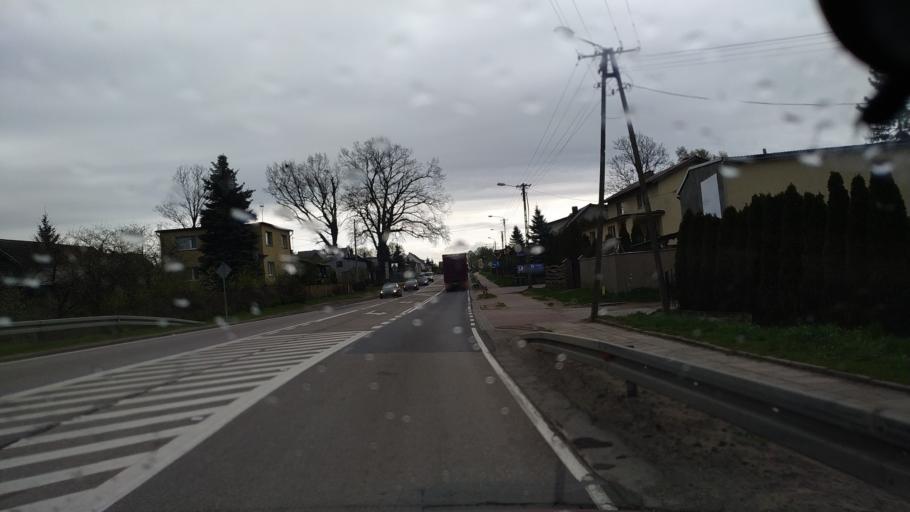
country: PL
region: Pomeranian Voivodeship
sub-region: Powiat starogardzki
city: Zblewo
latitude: 53.9205
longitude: 18.2806
